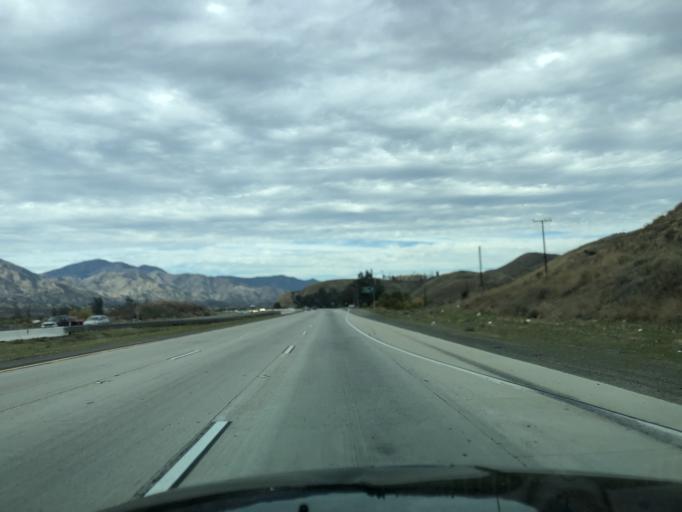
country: US
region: California
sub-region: Riverside County
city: Lake Elsinore
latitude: 33.7294
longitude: -117.3859
